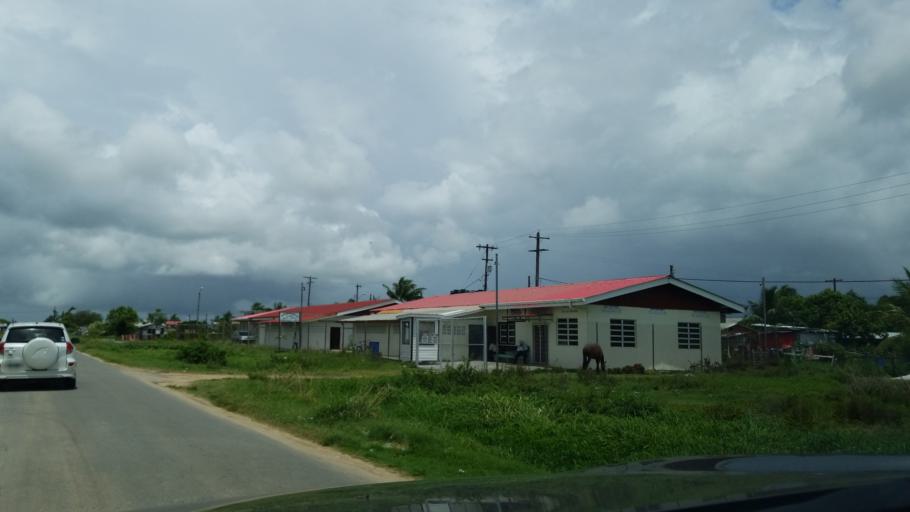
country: GY
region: Demerara-Mahaica
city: Georgetown
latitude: 6.8036
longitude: -58.1227
